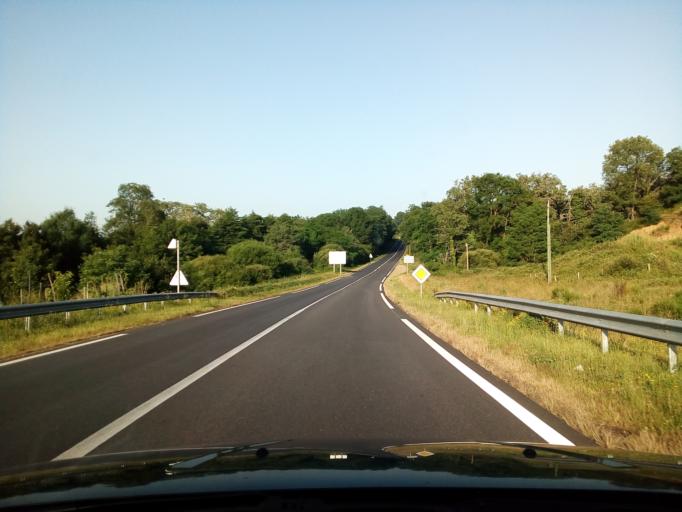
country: FR
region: Limousin
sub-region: Departement de la Haute-Vienne
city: Bussiere-Poitevine
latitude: 46.1087
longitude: 0.8924
